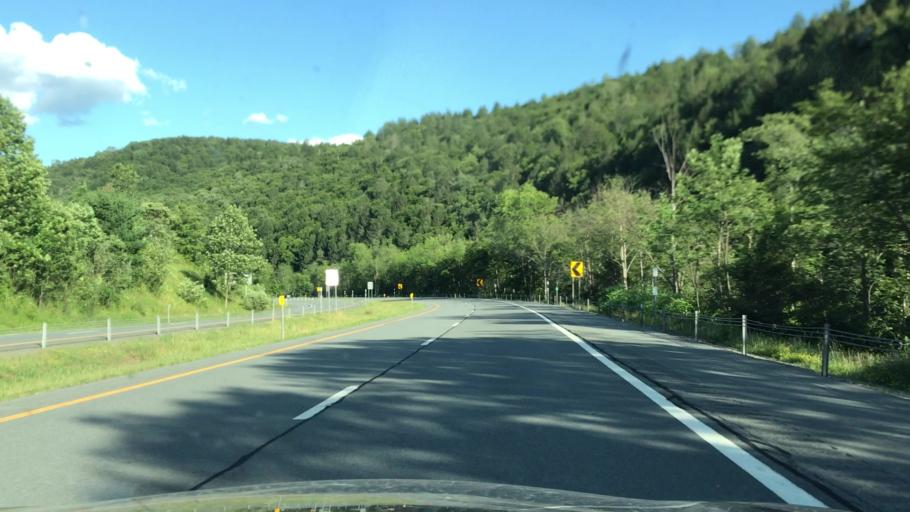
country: US
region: New York
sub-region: Sullivan County
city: Livingston Manor
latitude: 41.9256
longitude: -74.8979
